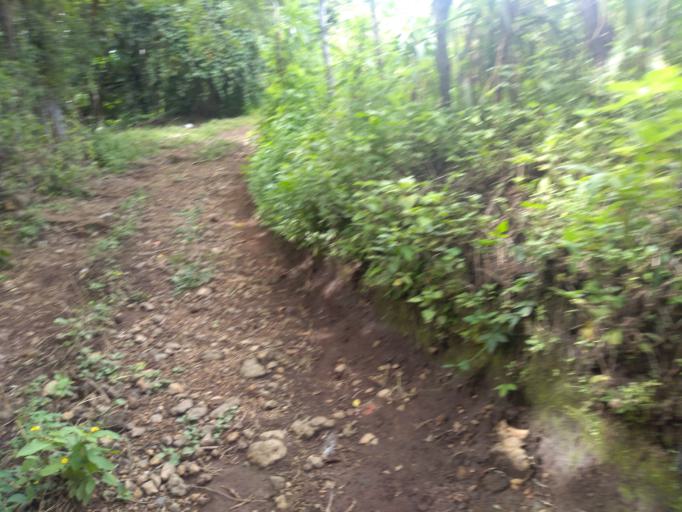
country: GT
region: Escuintla
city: San Vicente Pacaya
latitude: 14.3733
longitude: -90.5713
